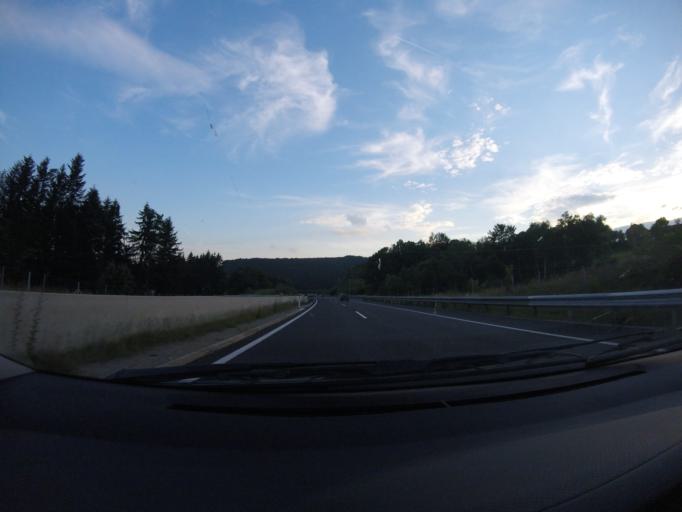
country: AT
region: Lower Austria
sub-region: Politischer Bezirk Neunkirchen
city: Zobern
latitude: 47.4975
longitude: 16.1020
